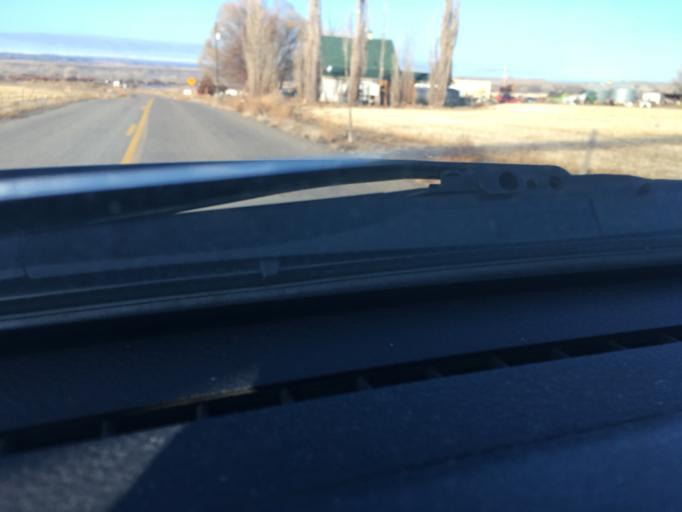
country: US
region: Colorado
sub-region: Delta County
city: Delta
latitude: 38.7483
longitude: -108.1364
